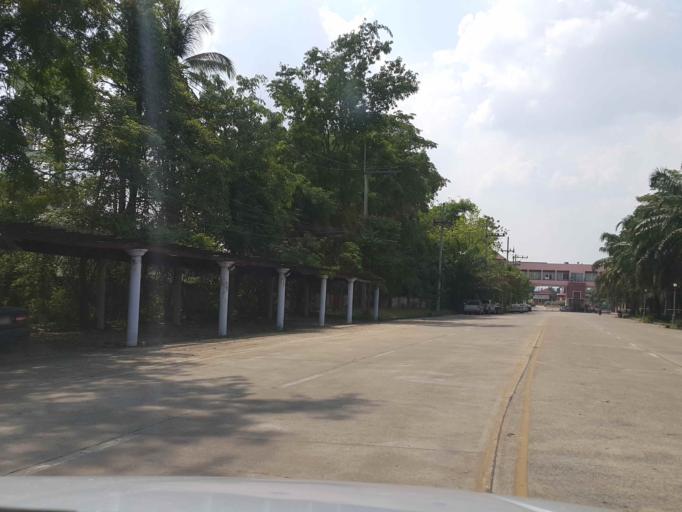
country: TH
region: Chiang Mai
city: Hang Dong
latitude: 18.7037
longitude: 98.9365
